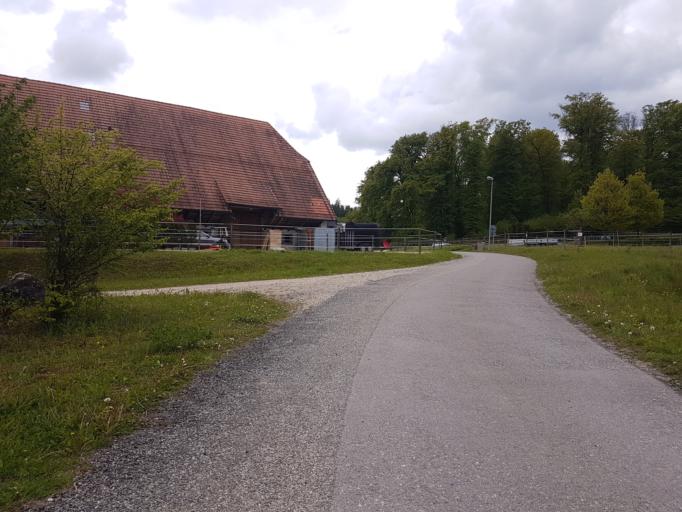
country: CH
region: Solothurn
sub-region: Bezirk Solothurn
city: Solothurn
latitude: 47.1956
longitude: 7.5302
